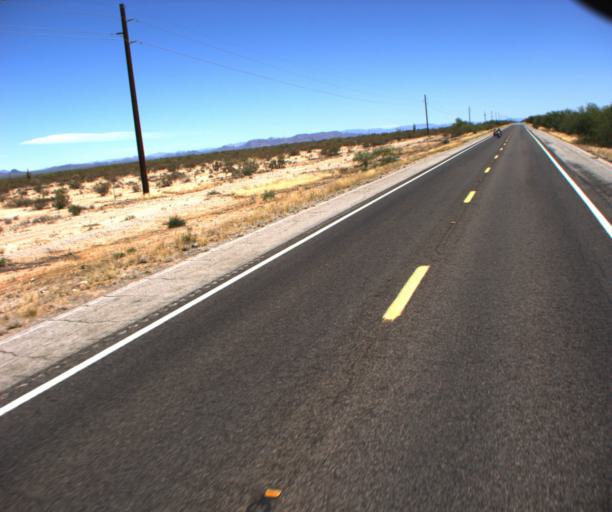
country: US
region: Arizona
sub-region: La Paz County
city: Salome
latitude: 33.8886
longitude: -113.3401
